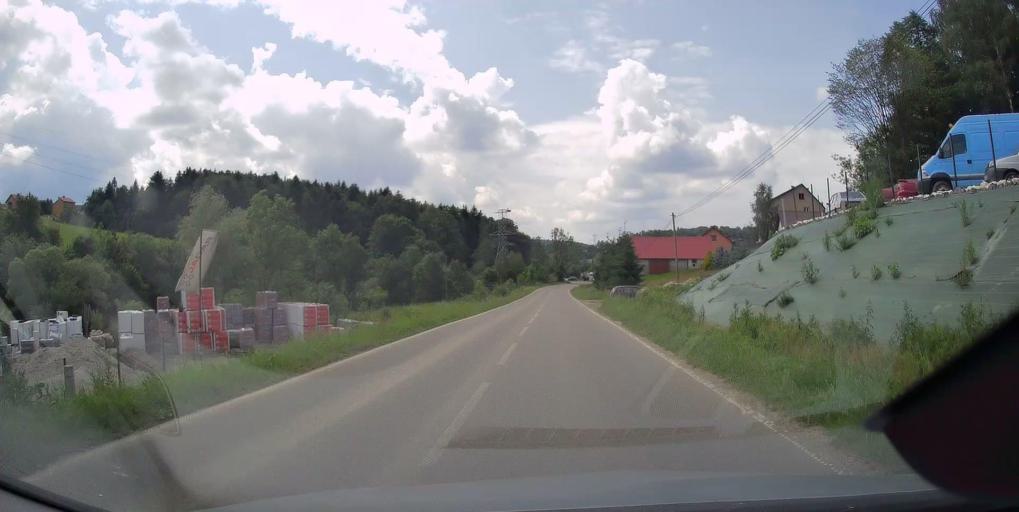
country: PL
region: Lesser Poland Voivodeship
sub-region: Powiat nowosadecki
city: Korzenna
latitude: 49.6709
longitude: 20.7759
